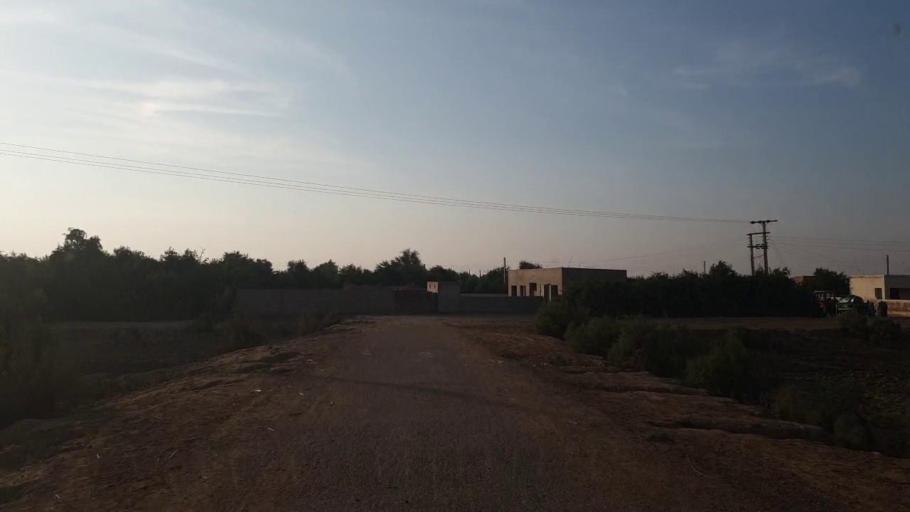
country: PK
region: Sindh
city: Sann
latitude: 25.9263
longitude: 68.1744
